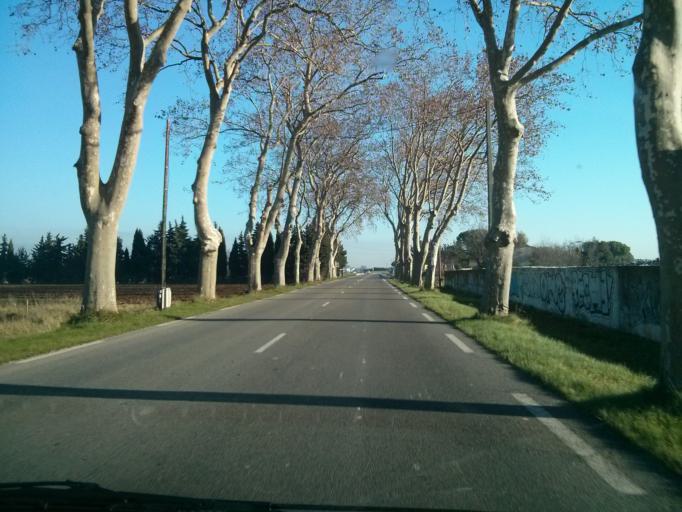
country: FR
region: Languedoc-Roussillon
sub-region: Departement du Gard
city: Codognan
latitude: 43.7324
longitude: 4.2310
